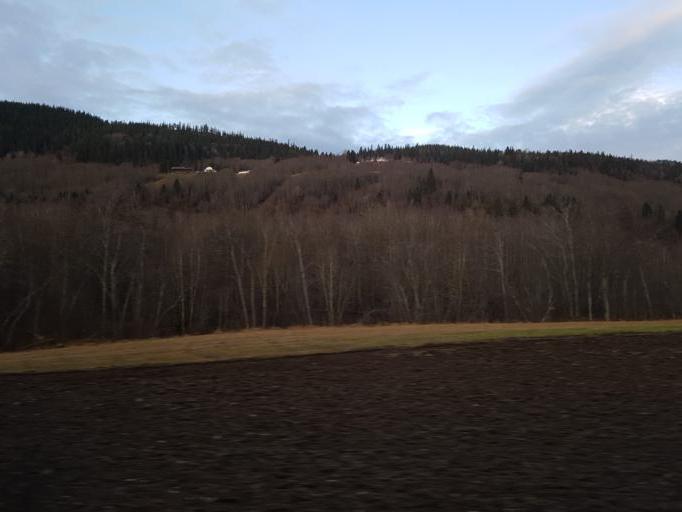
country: NO
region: Sor-Trondelag
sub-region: Melhus
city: Lundamo
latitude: 63.1613
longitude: 10.2950
